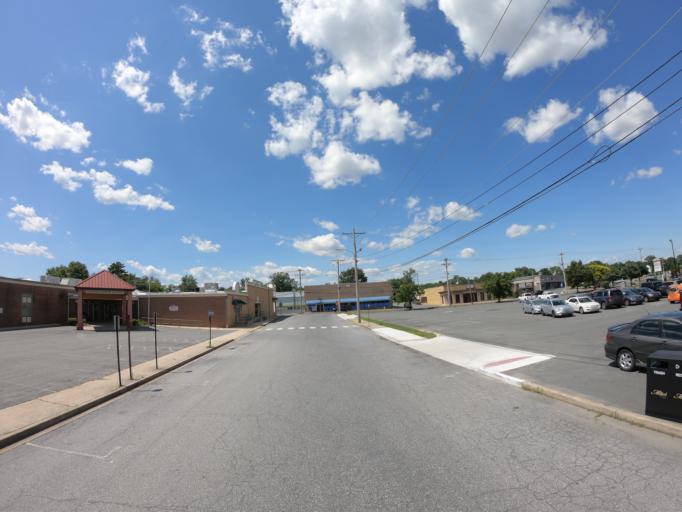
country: US
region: Delaware
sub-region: Sussex County
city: Milford
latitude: 38.9140
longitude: -75.4265
